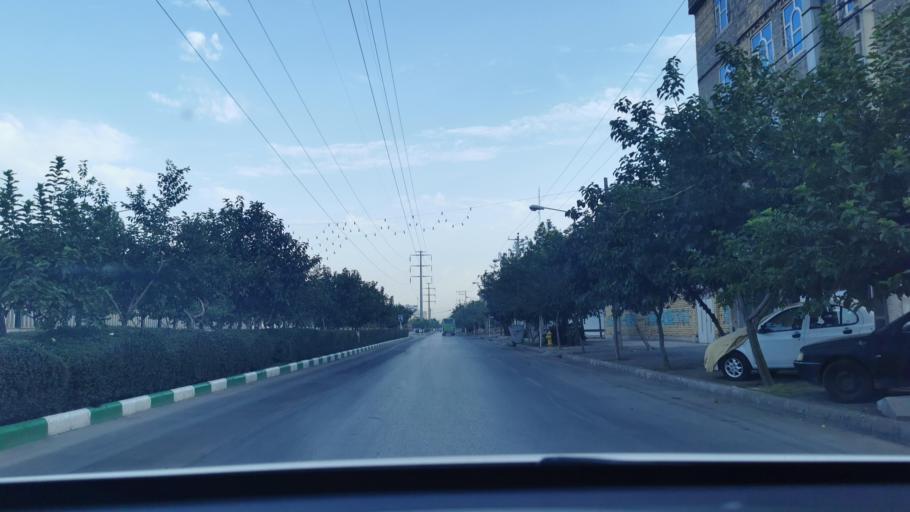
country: IR
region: Razavi Khorasan
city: Mashhad
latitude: 36.3522
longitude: 59.5294
